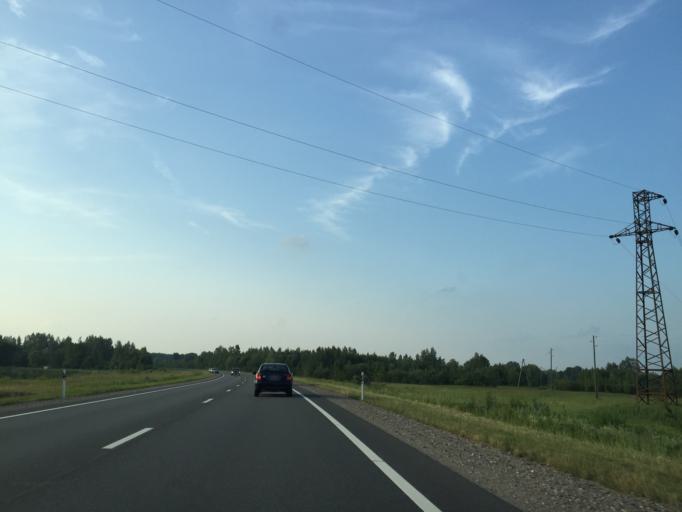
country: LV
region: Ozolnieku
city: Ozolnieki
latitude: 56.6695
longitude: 23.8235
